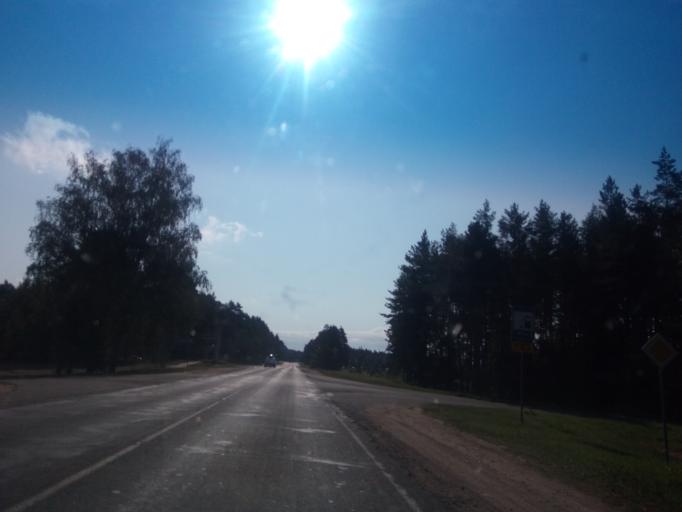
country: BY
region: Vitebsk
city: Vyerkhnyadzvinsk
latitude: 55.7581
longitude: 27.9503
